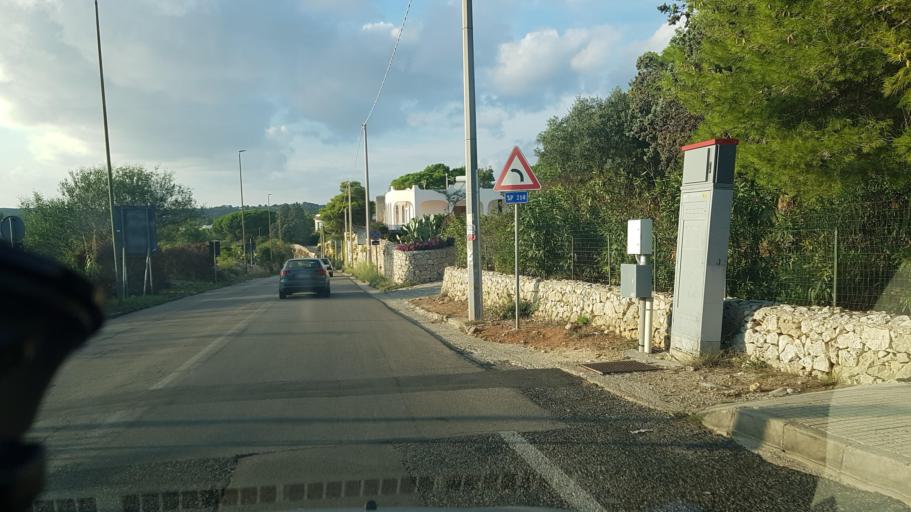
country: IT
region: Apulia
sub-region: Provincia di Lecce
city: Leuca
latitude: 39.7989
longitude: 18.3680
